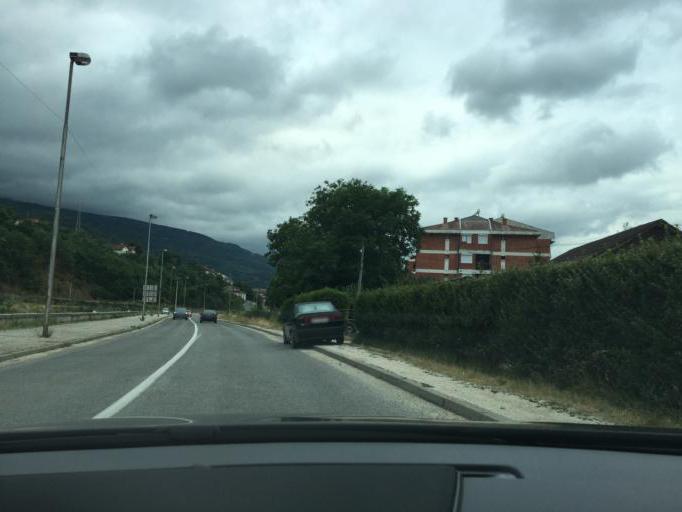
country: MK
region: Kriva Palanka
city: Kriva Palanka
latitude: 42.2108
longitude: 22.3412
